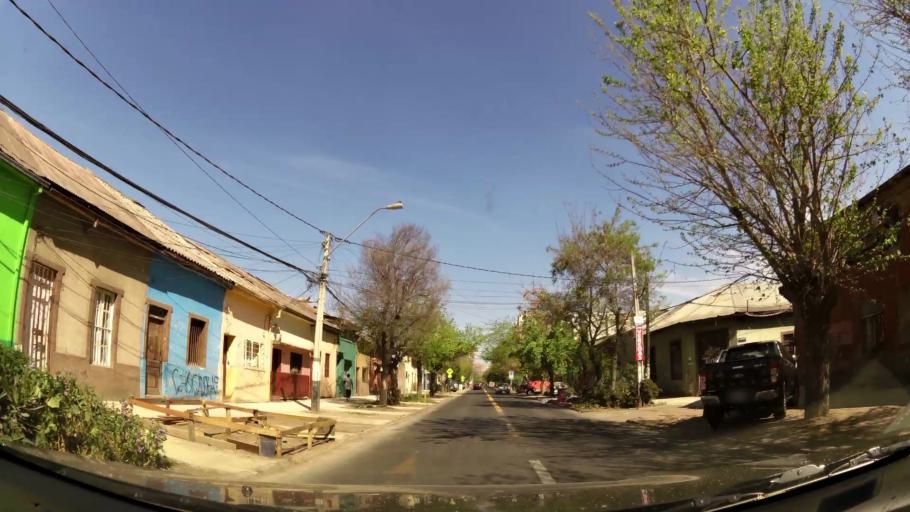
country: CL
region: Santiago Metropolitan
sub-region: Provincia de Santiago
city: Santiago
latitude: -33.4217
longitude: -70.6603
